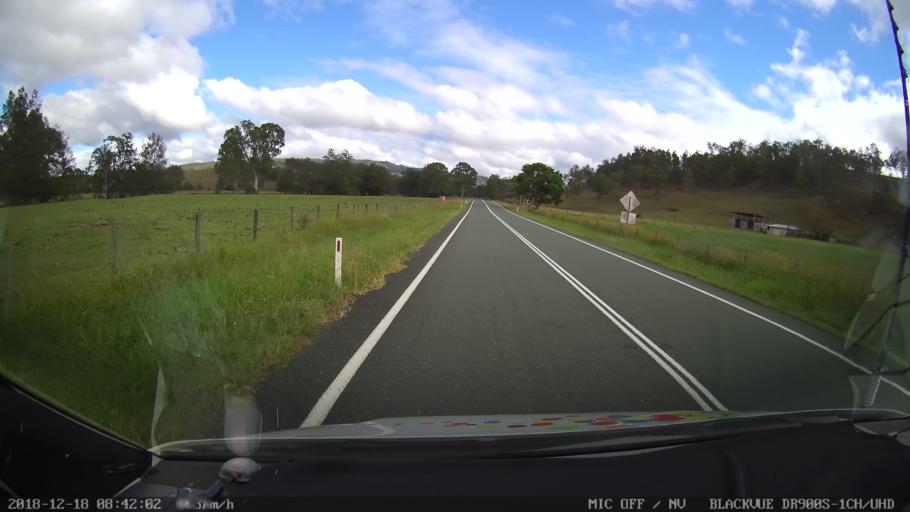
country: AU
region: Queensland
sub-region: Logan
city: Cedar Vale
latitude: -28.2311
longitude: 152.8605
